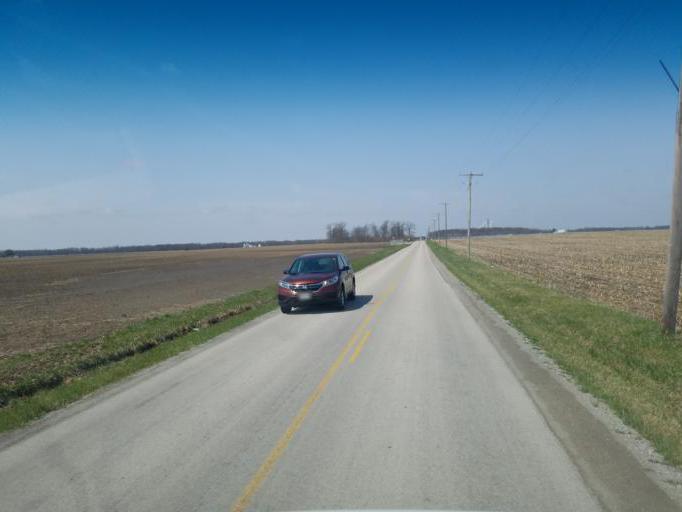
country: US
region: Ohio
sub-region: Wyandot County
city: Upper Sandusky
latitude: 40.8762
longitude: -83.3046
